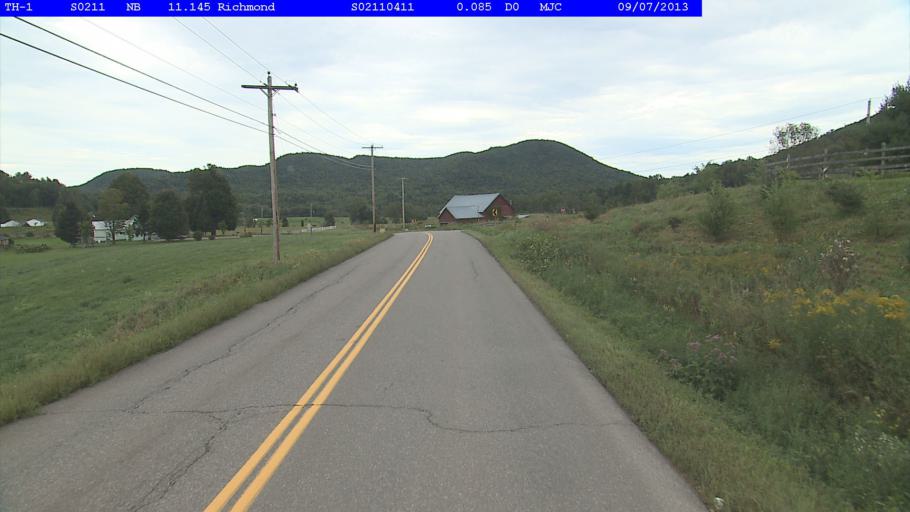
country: US
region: Vermont
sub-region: Chittenden County
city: Williston
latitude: 44.3546
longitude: -72.9924
